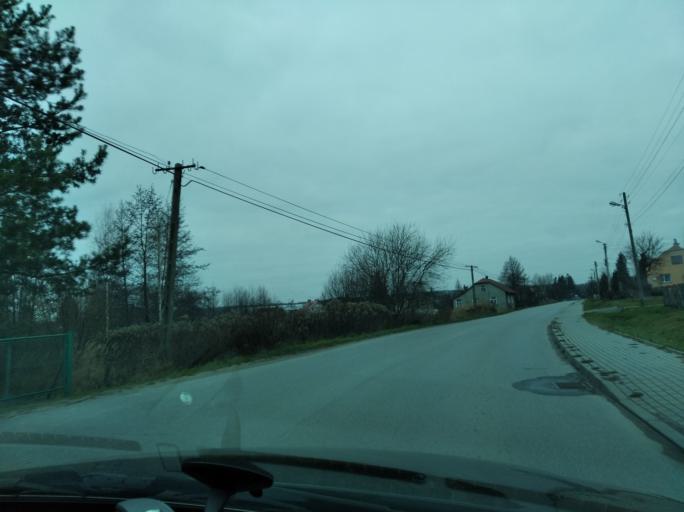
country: PL
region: Subcarpathian Voivodeship
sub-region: Powiat lancucki
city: Rakszawa
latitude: 50.1667
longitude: 22.2342
